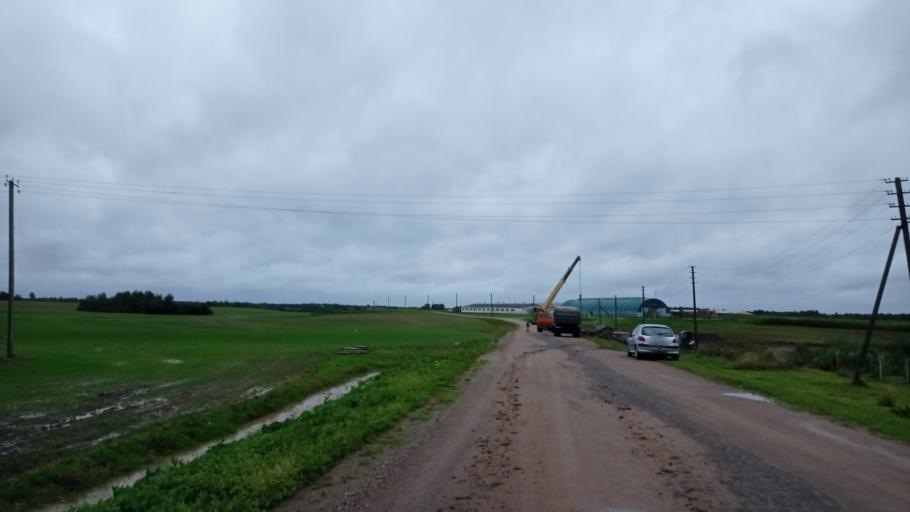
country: BY
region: Vitebsk
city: Haradok
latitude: 55.3404
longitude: 30.0964
